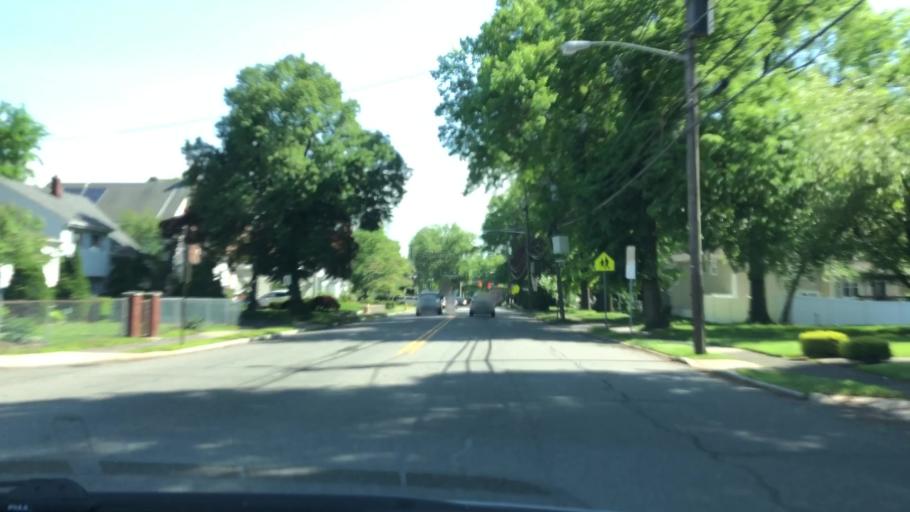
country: US
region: New Jersey
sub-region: Essex County
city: Brookdale
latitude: 40.8309
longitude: -74.1735
